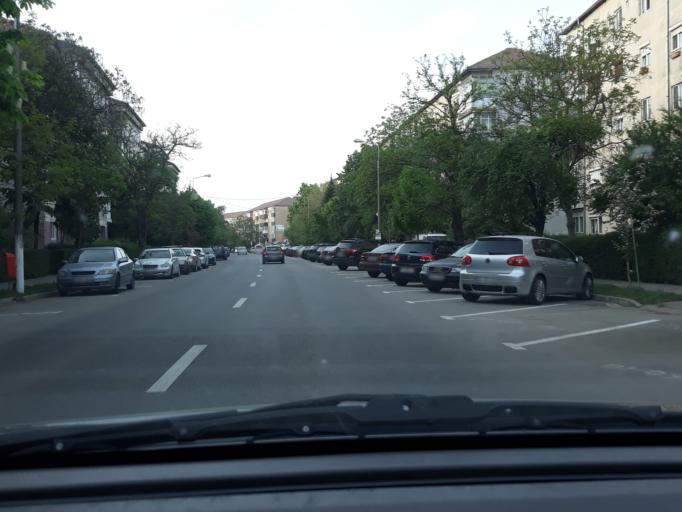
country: RO
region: Bihor
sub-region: Comuna Sanmartin
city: Sanmartin
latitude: 47.0310
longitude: 21.9585
